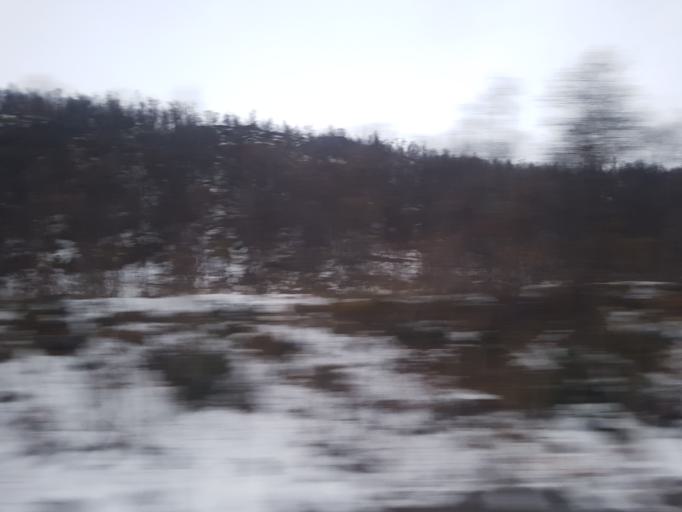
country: NO
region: Sor-Trondelag
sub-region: Oppdal
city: Oppdal
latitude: 62.3007
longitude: 9.6026
